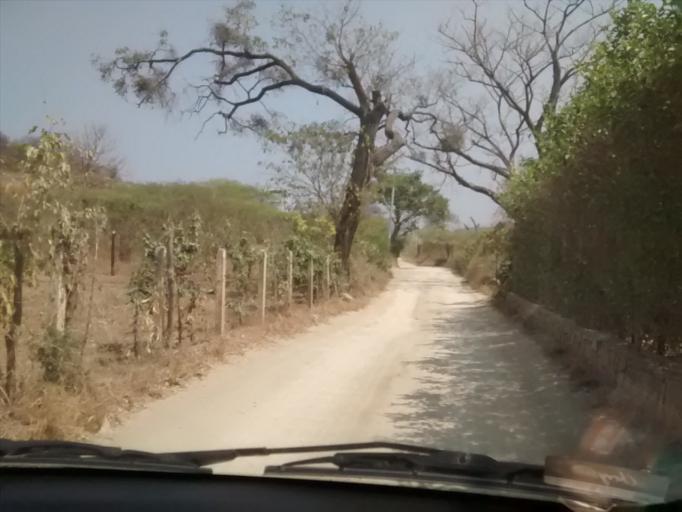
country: CO
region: Magdalena
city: Santa Marta
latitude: 11.1639
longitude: -74.2175
